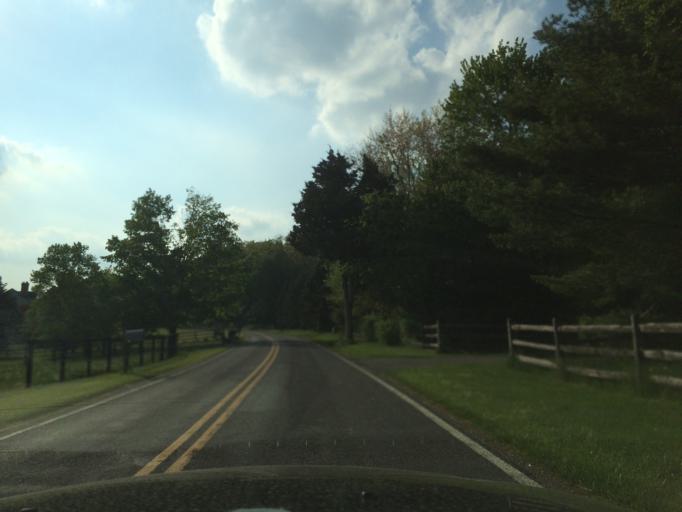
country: US
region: Maryland
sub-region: Carroll County
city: Mount Airy
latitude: 39.2968
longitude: -77.0846
